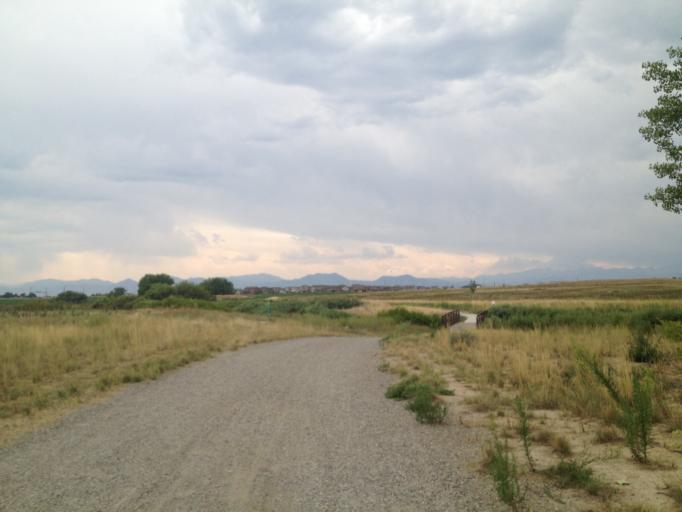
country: US
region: Colorado
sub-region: Boulder County
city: Erie
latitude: 40.0193
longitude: -105.0486
